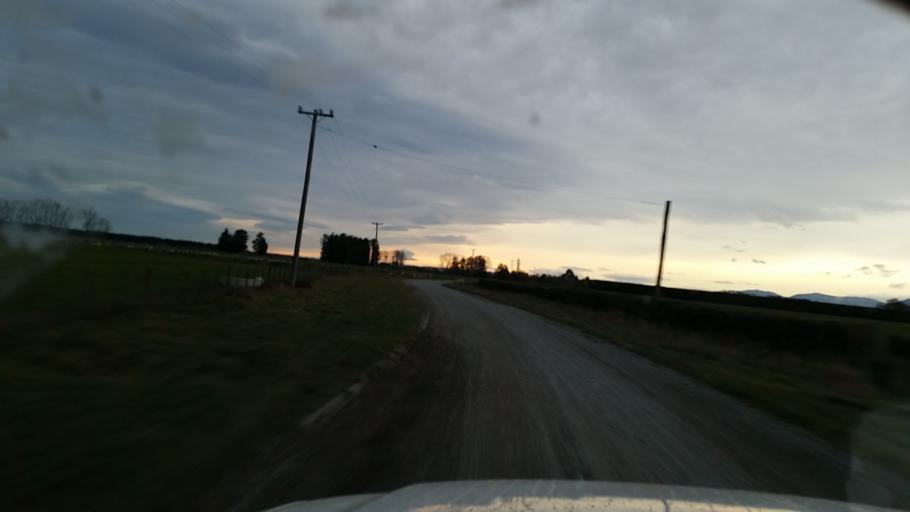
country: NZ
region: Canterbury
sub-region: Ashburton District
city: Ashburton
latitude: -43.8278
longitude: 171.6355
